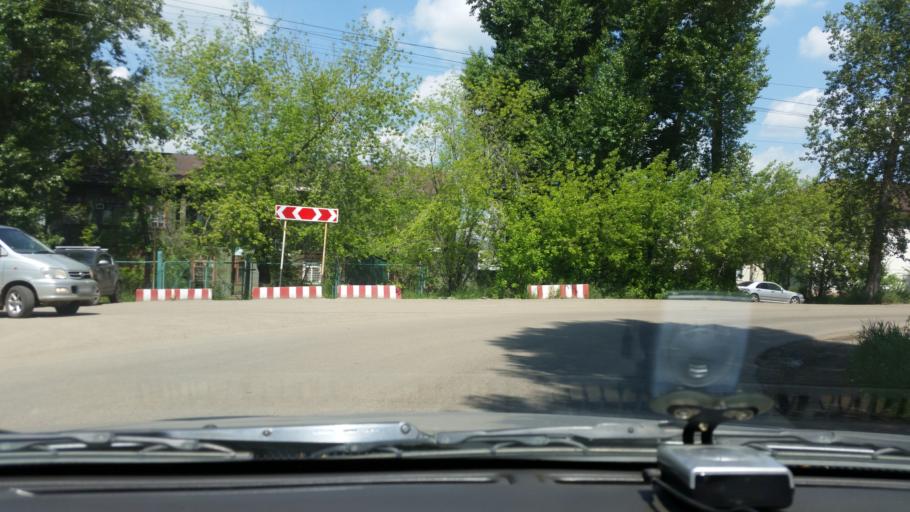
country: RU
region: Irkutsk
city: Dzerzhinsk
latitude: 52.2810
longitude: 104.3789
